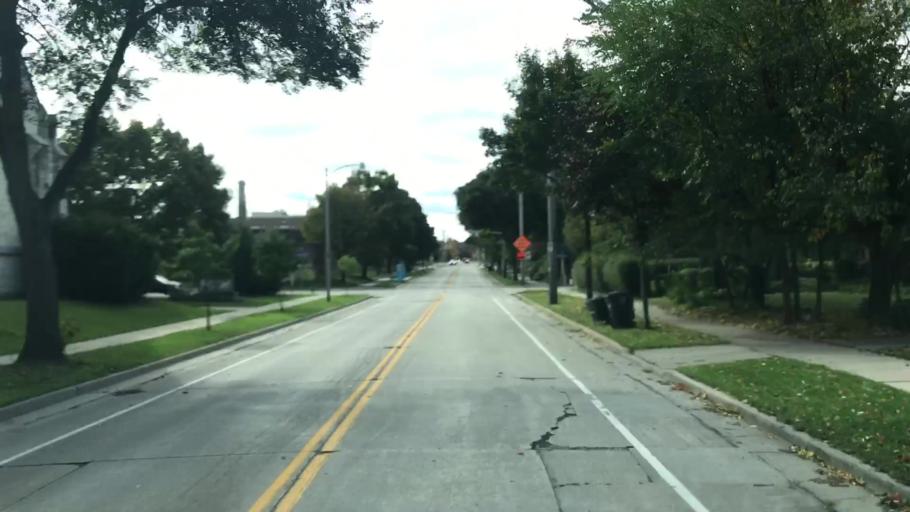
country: US
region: Wisconsin
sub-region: Milwaukee County
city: Wauwatosa
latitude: 43.0558
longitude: -88.0074
